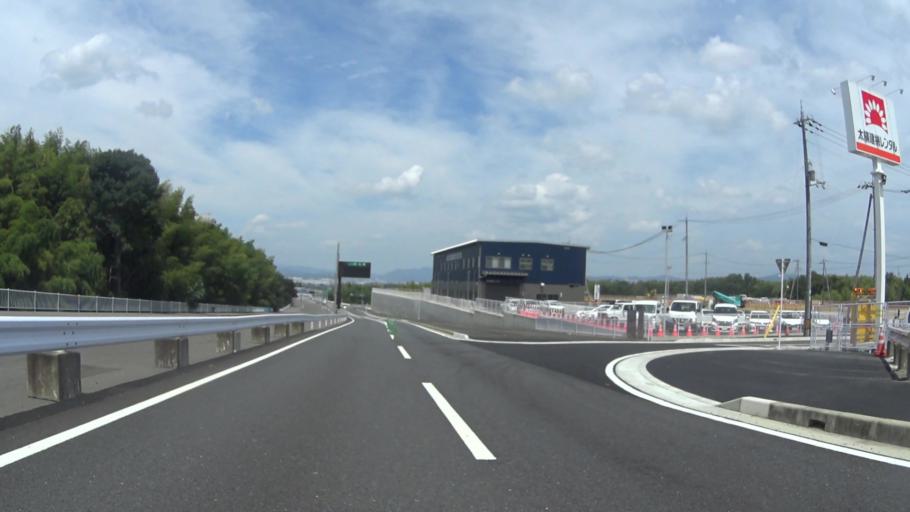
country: JP
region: Kyoto
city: Yawata
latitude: 34.8455
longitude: 135.7196
